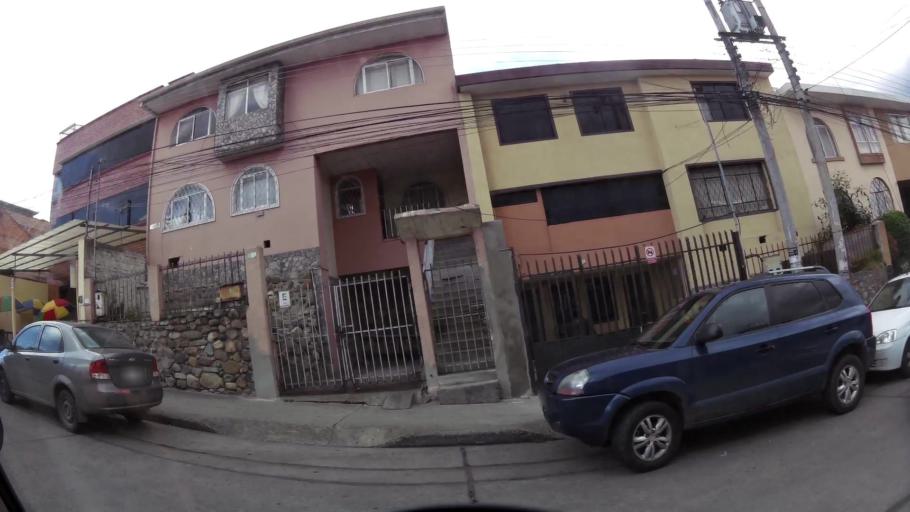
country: EC
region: Azuay
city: Cuenca
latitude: -2.8858
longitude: -79.0063
